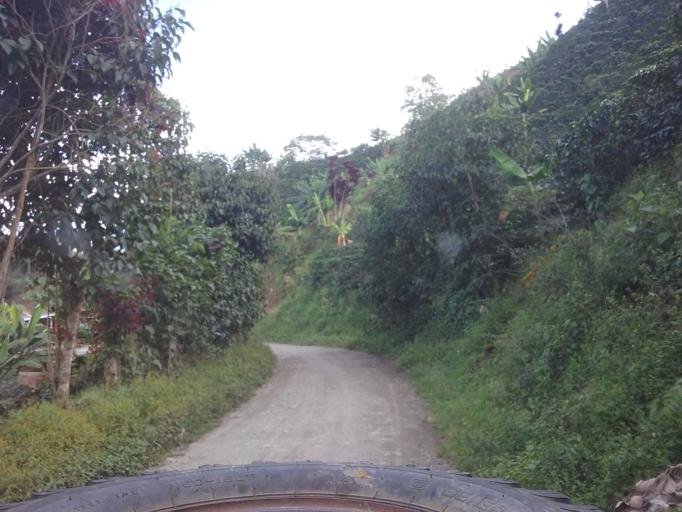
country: CO
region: Tolima
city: Libano
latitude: 4.8122
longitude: -75.0390
